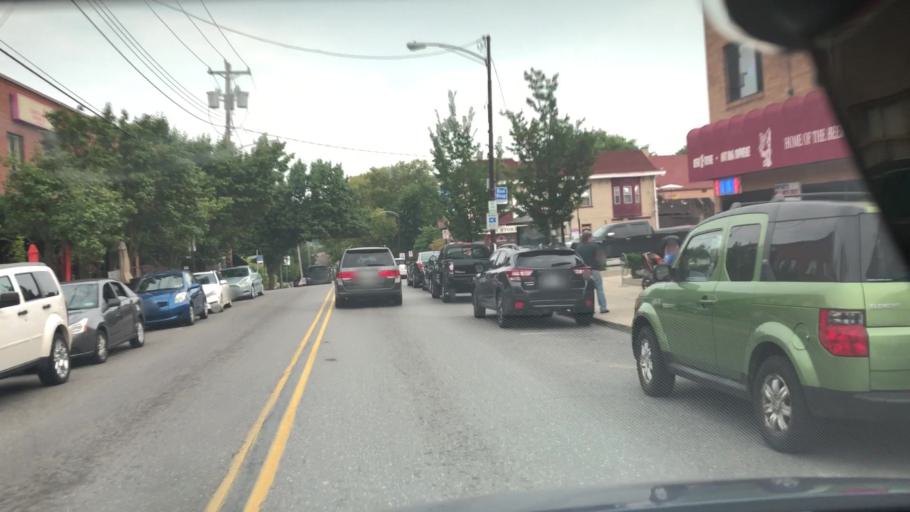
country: US
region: Pennsylvania
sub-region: Allegheny County
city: Edgewood
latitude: 40.4322
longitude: -79.8936
